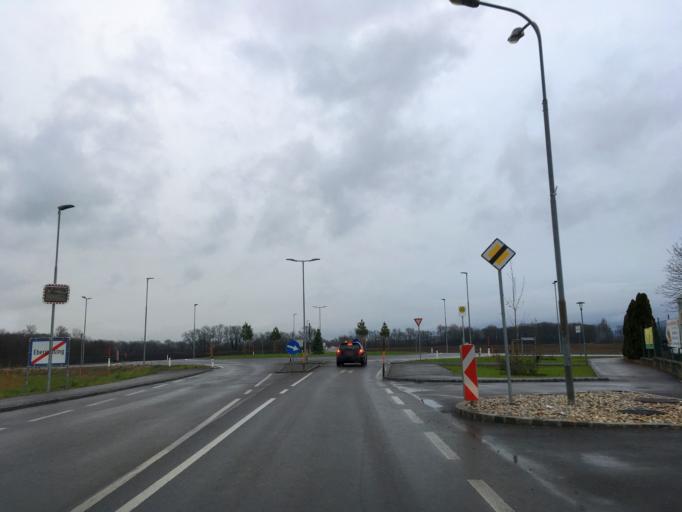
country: AT
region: Lower Austria
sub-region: Politischer Bezirk Wien-Umgebung
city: Ebergassing
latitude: 48.0431
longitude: 16.5235
